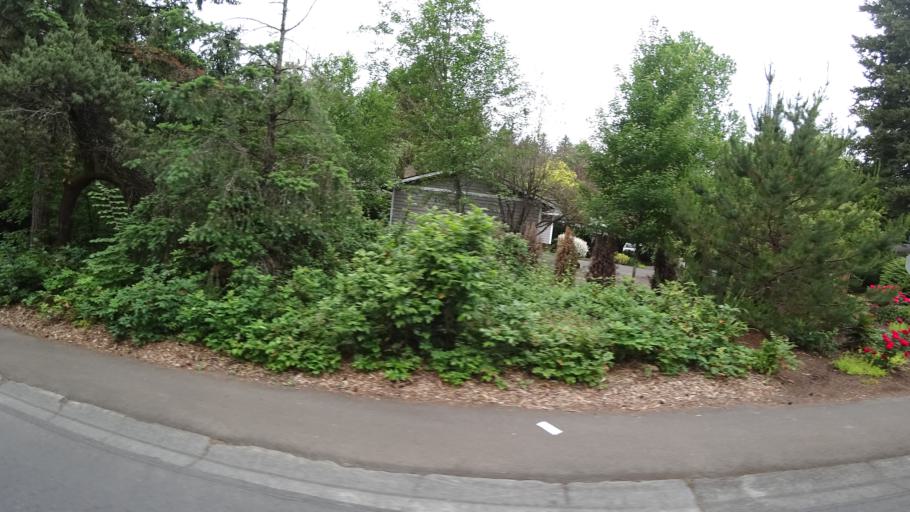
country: US
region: Oregon
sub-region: Clackamas County
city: Lake Oswego
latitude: 45.4320
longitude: -122.7074
